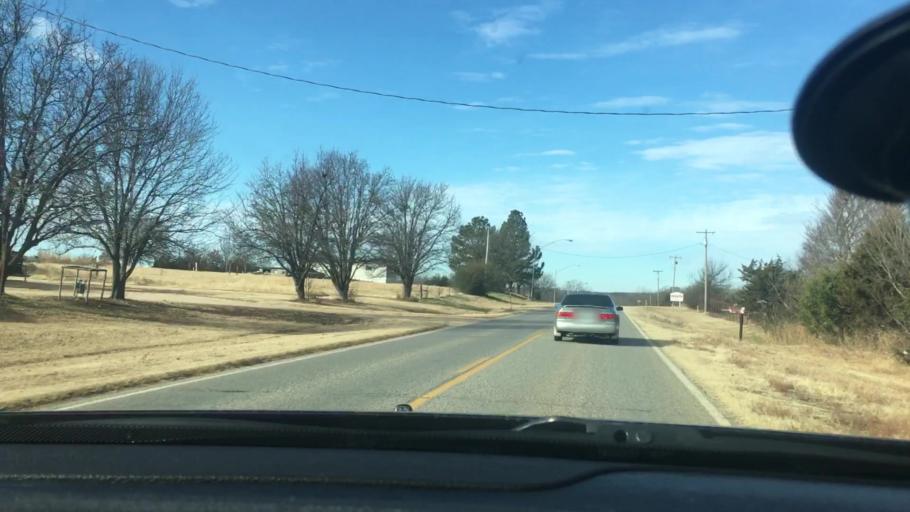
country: US
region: Oklahoma
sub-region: Seminole County
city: Konawa
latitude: 34.9495
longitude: -96.7448
